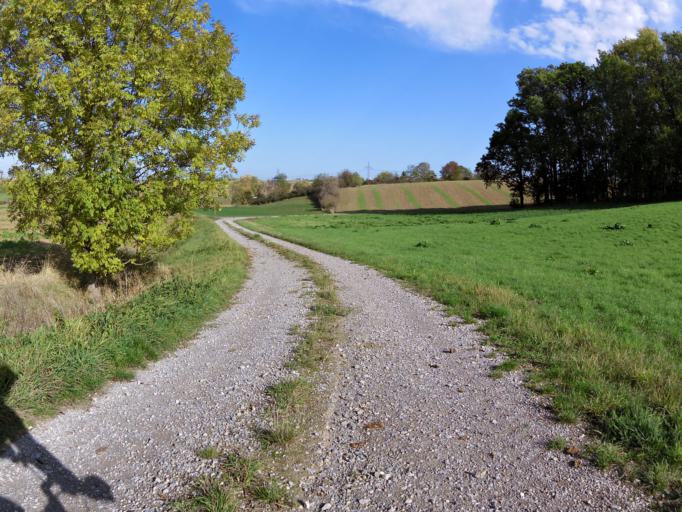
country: DE
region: Bavaria
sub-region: Regierungsbezirk Unterfranken
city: Theilheim
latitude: 49.7546
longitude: 10.0581
